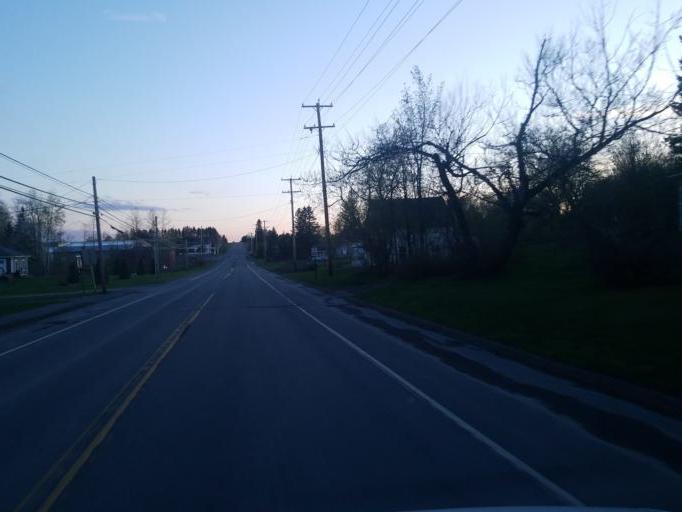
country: US
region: Maine
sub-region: Aroostook County
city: Caribou
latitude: 46.8558
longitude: -68.0259
